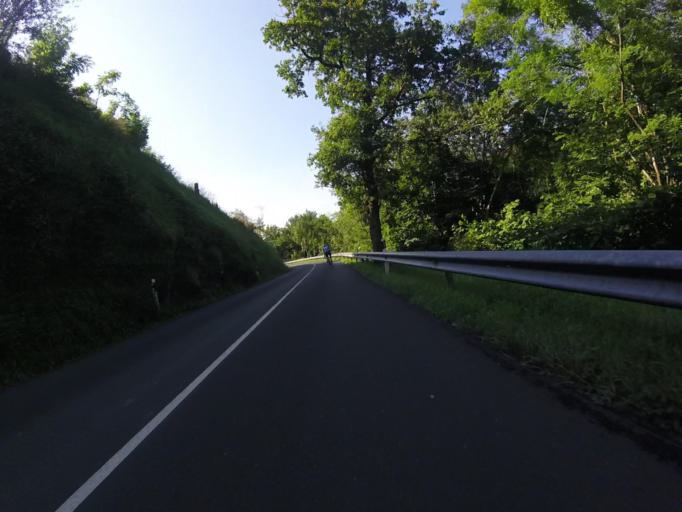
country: ES
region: Basque Country
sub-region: Provincia de Guipuzcoa
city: Asteasu
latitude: 43.2067
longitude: -2.1141
